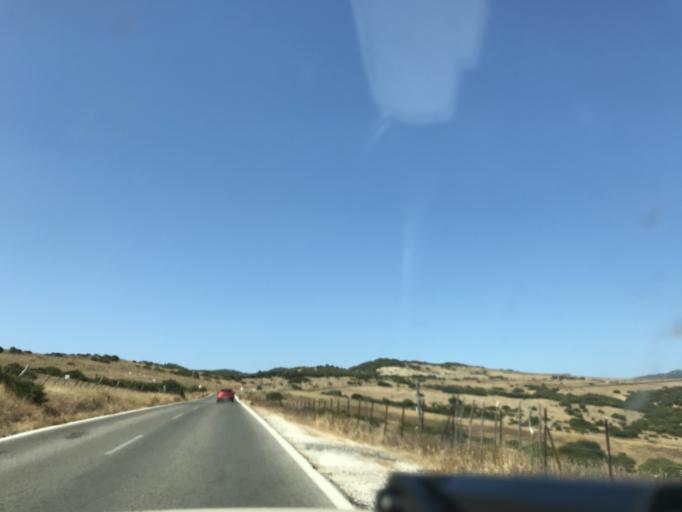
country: ES
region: Andalusia
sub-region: Provincia de Cadiz
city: Zahara de los Atunes
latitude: 36.0970
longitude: -5.7495
